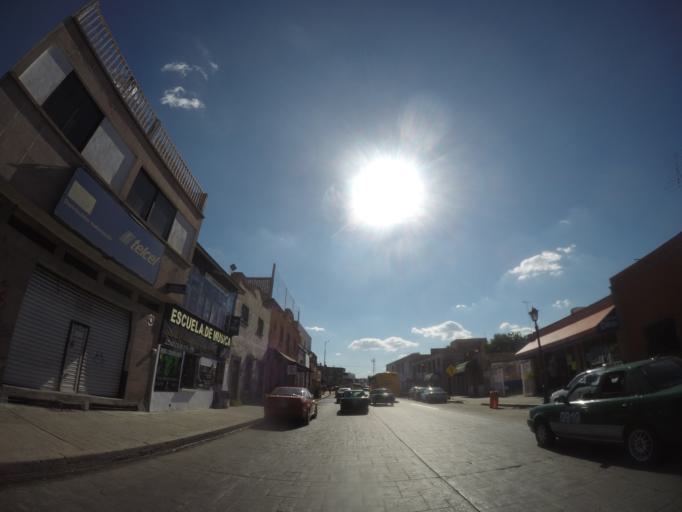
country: MX
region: San Luis Potosi
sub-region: San Luis Potosi
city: San Luis Potosi
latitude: 22.1583
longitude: -100.9736
